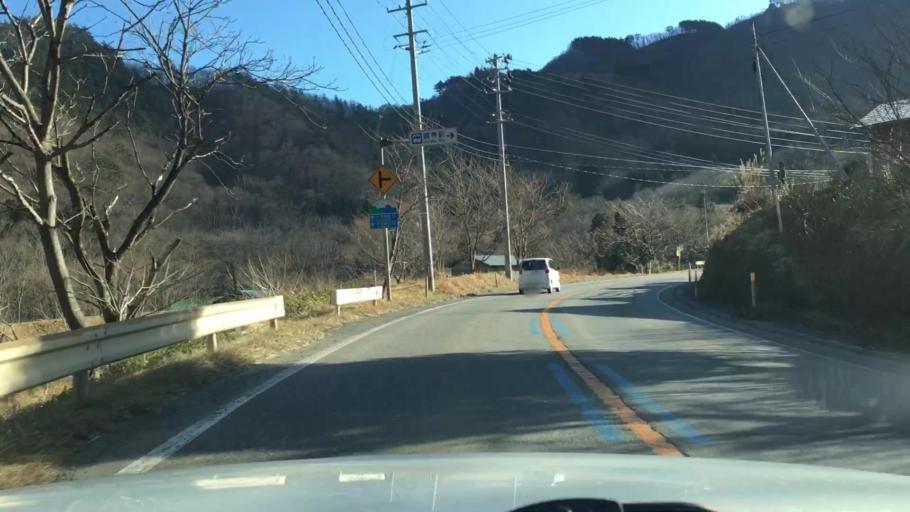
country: JP
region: Iwate
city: Miyako
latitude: 39.6047
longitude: 141.7728
